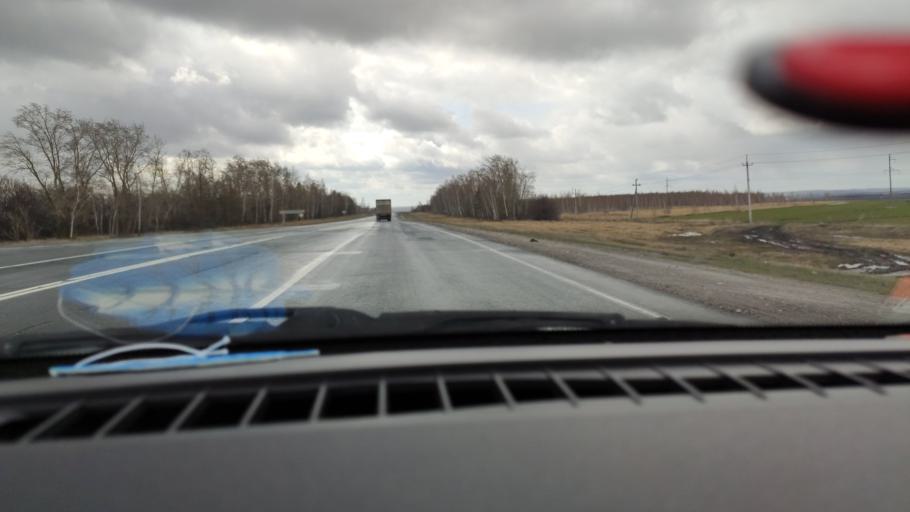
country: RU
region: Samara
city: Yelkhovka
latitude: 53.9374
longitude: 50.2635
